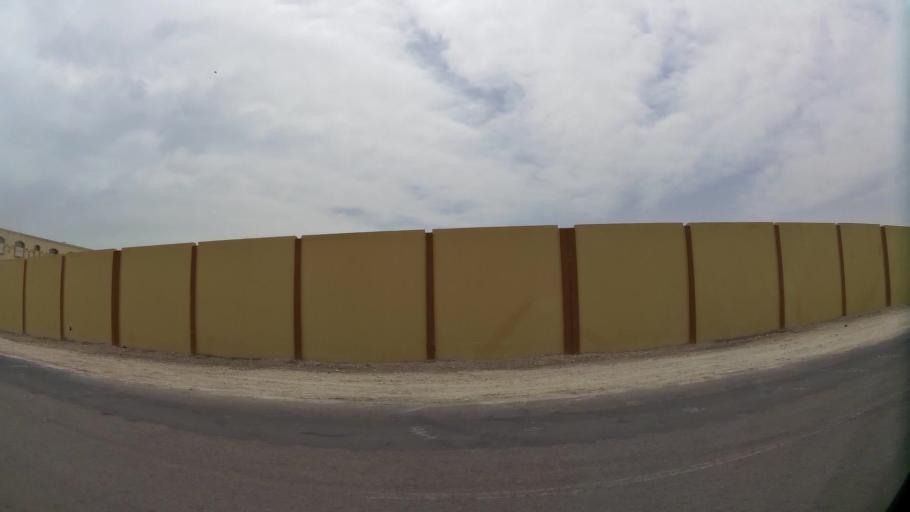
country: QA
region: Baladiyat ar Rayyan
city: Ar Rayyan
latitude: 25.2305
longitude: 51.4514
